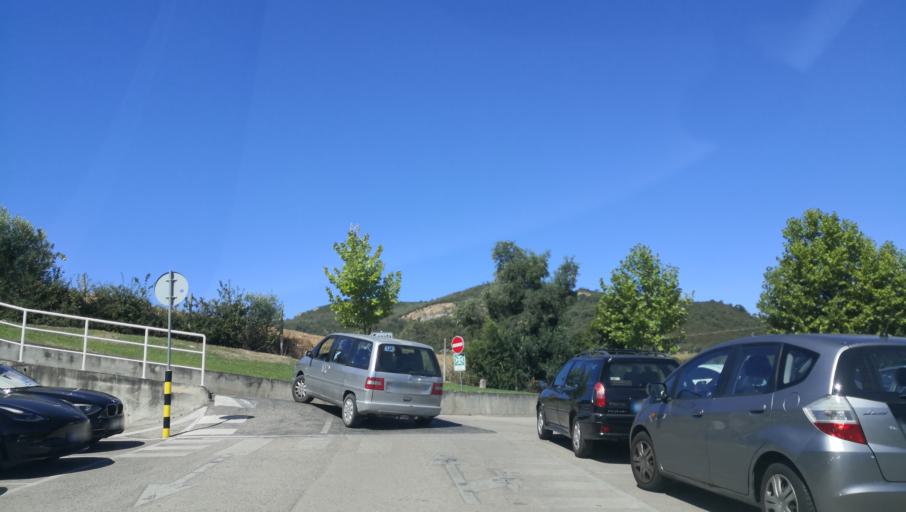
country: PT
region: Setubal
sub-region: Setubal
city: Setubal
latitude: 38.5337
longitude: -8.9103
